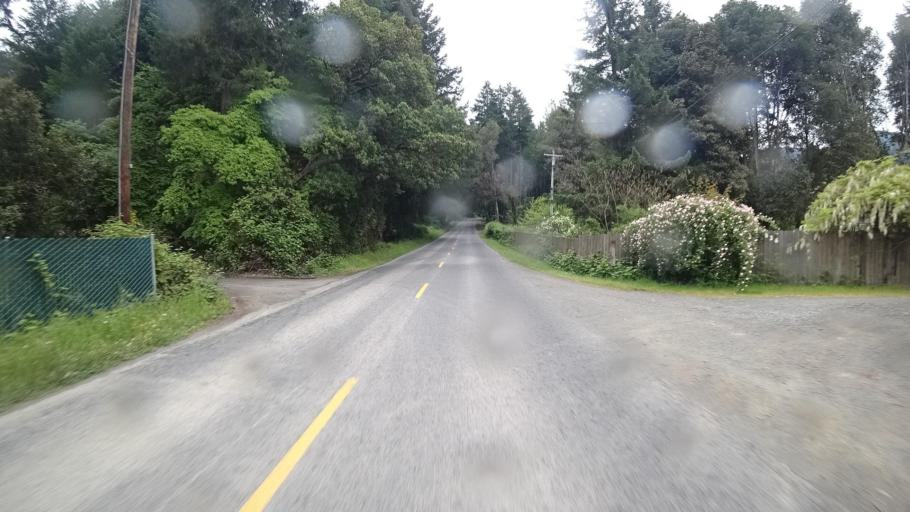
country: US
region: California
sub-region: Humboldt County
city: Willow Creek
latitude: 41.0562
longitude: -123.6727
